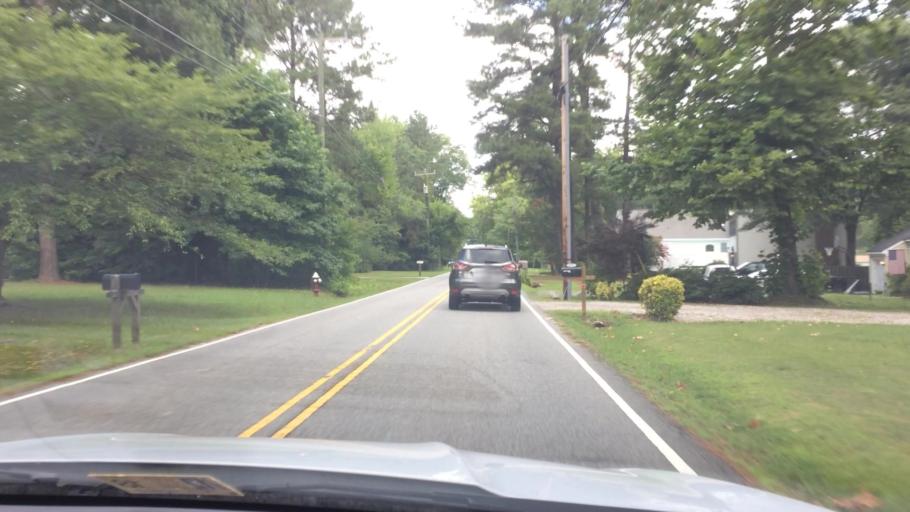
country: US
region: Virginia
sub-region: City of Poquoson
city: Poquoson
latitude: 37.1448
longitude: -76.4472
